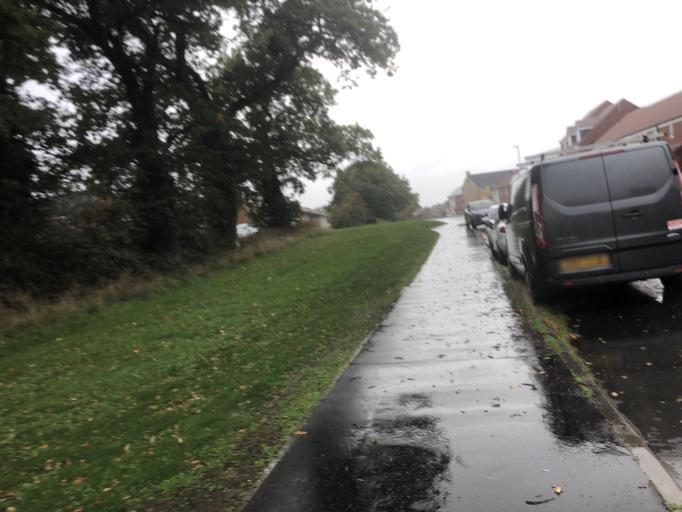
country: GB
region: England
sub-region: Norfolk
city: Spixworth
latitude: 52.6588
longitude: 1.3439
